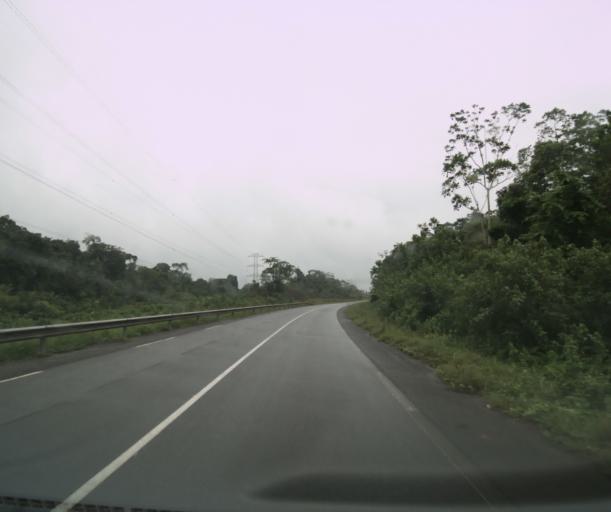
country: CM
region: Littoral
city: Dizangue
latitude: 3.3612
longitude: 10.1029
